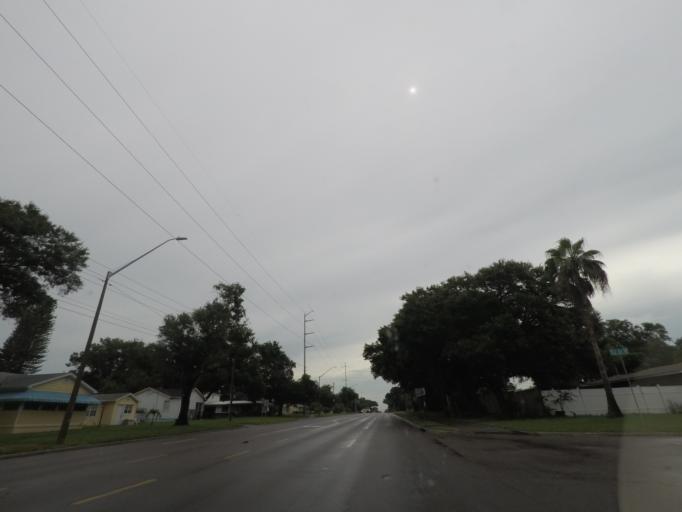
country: US
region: Florida
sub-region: Pinellas County
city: Kenneth City
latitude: 27.8064
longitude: -82.7063
